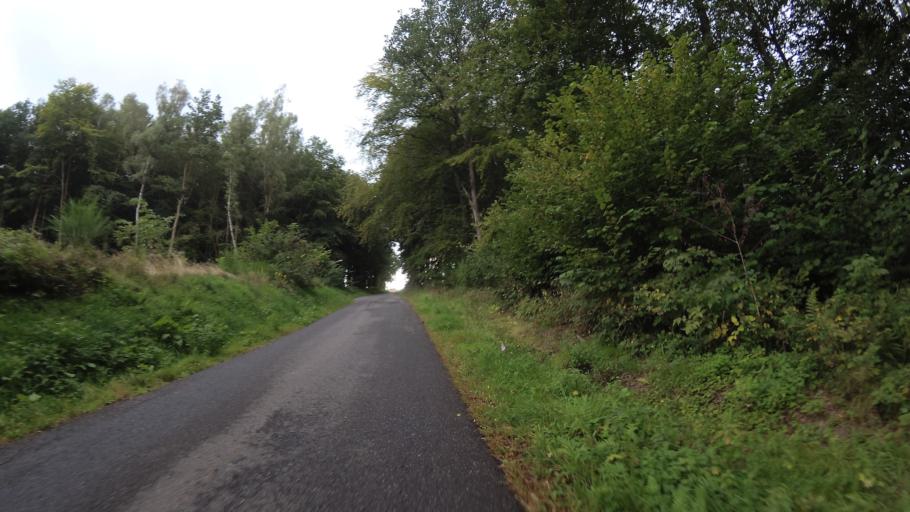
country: DE
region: Rheinland-Pfalz
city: Reichweiler
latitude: 49.5115
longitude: 7.2551
